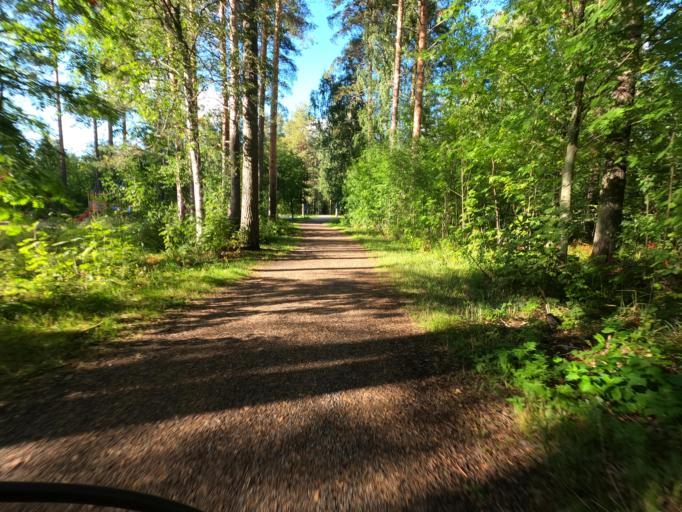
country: FI
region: North Karelia
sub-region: Joensuu
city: Joensuu
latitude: 62.6130
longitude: 29.7463
